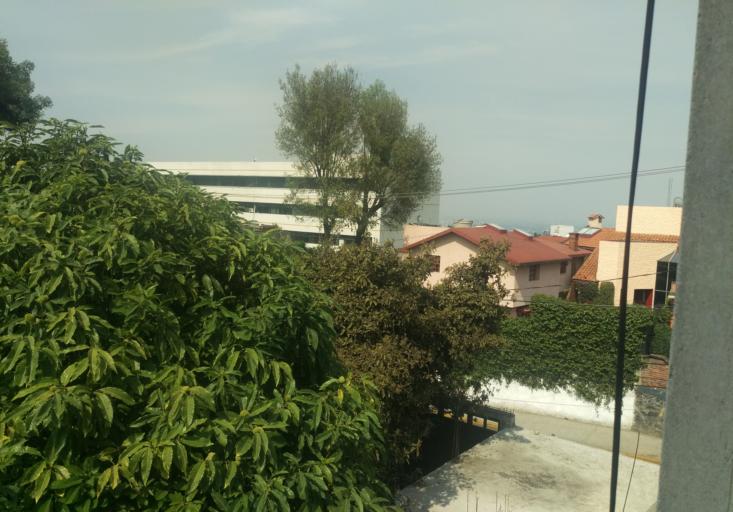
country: MX
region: Mexico City
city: Magdalena Contreras
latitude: 19.3035
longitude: -99.2489
